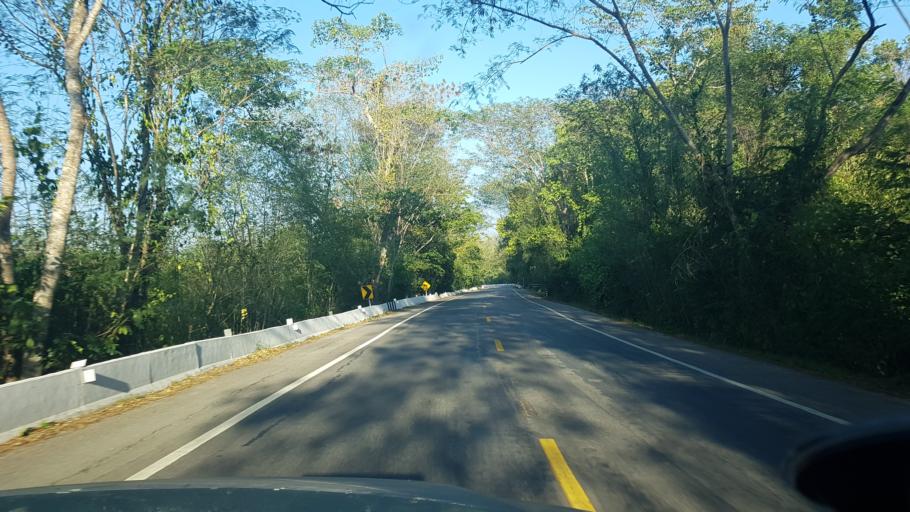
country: TH
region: Khon Kaen
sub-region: Amphoe Phu Pha Man
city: Phu Pha Man
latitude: 16.6481
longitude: 101.7784
